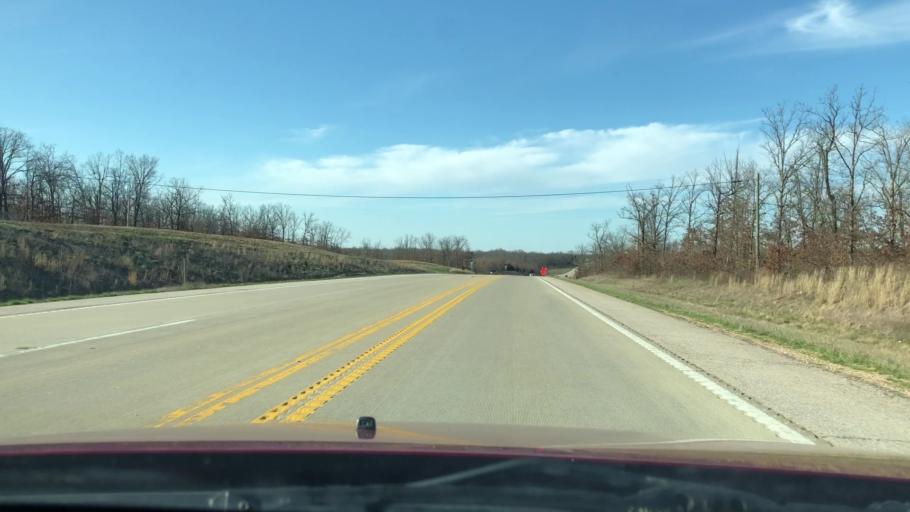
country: US
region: Missouri
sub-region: Camden County
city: Camdenton
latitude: 37.9366
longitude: -92.7152
